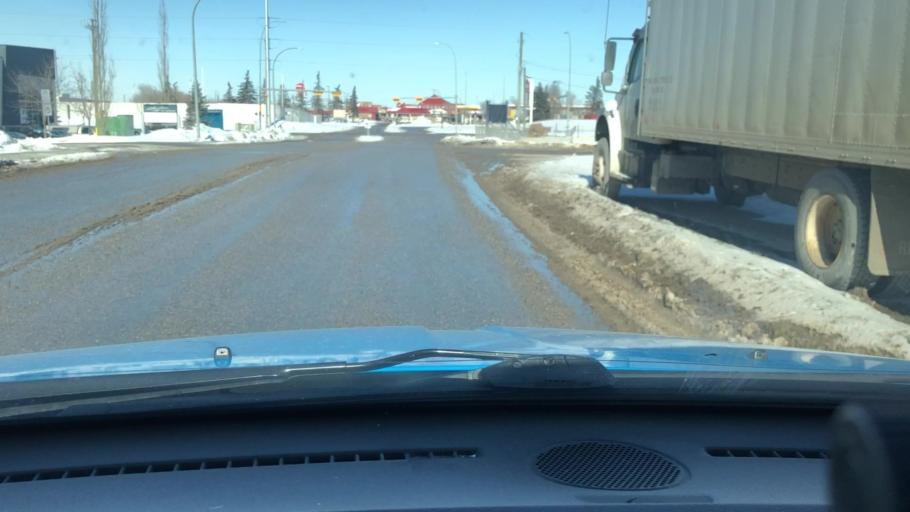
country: CA
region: Alberta
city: Calgary
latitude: 51.0074
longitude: -114.0041
